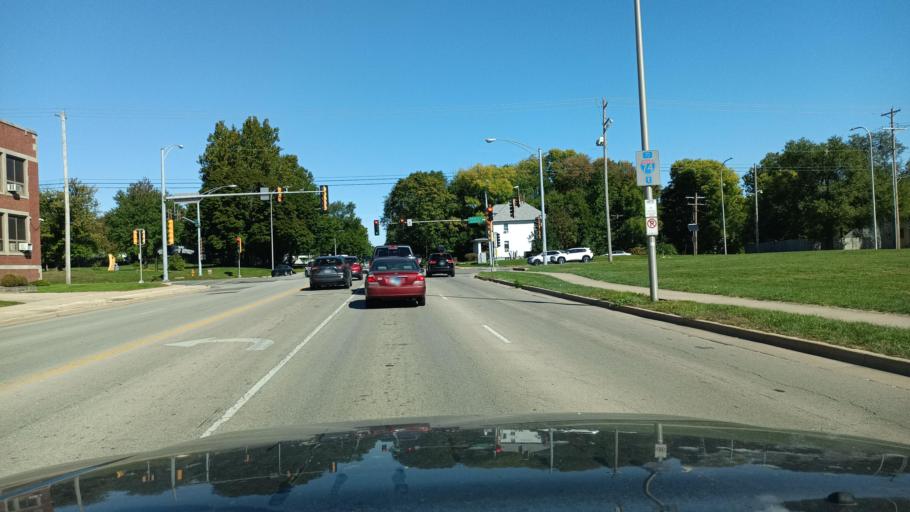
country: US
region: Illinois
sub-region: Champaign County
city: Champaign
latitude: 40.1265
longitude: -88.2435
